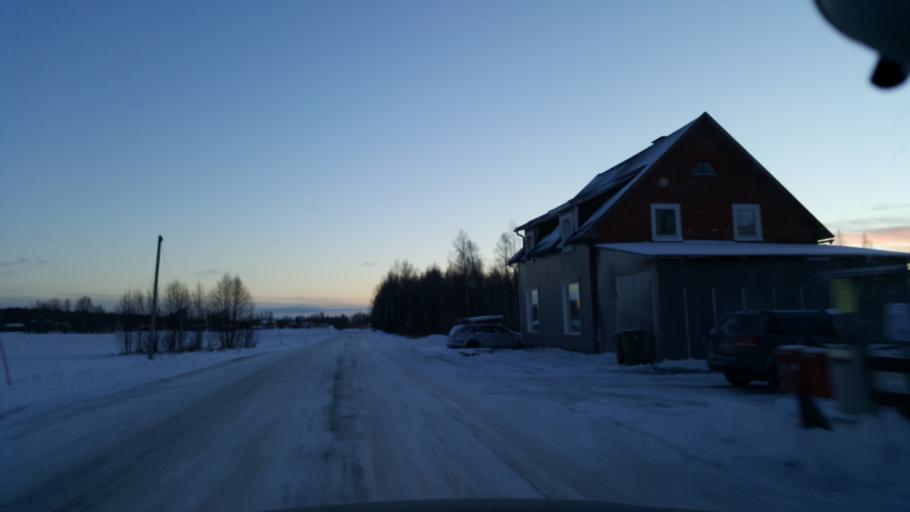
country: SE
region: Norrbotten
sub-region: Lulea Kommun
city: Sodra Sunderbyn
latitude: 65.5384
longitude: 21.9038
